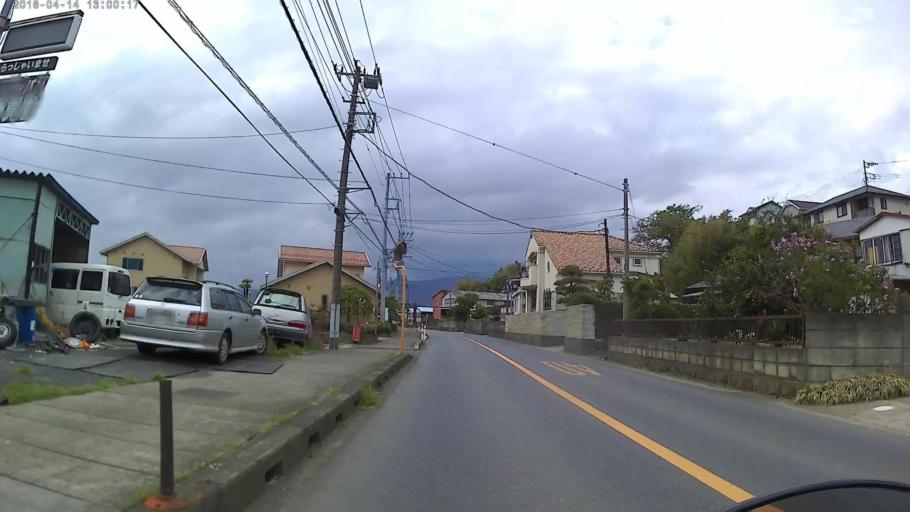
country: JP
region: Kanagawa
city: Isehara
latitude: 35.3718
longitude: 139.3066
